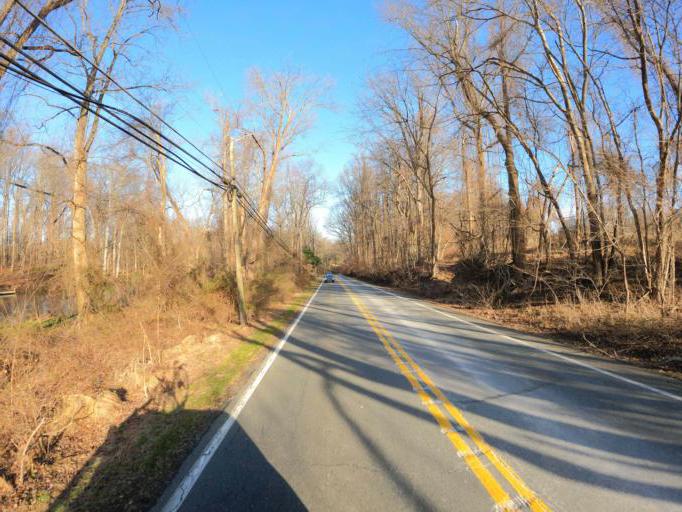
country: US
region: Maryland
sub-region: Montgomery County
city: Olney
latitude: 39.1942
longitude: -77.0667
